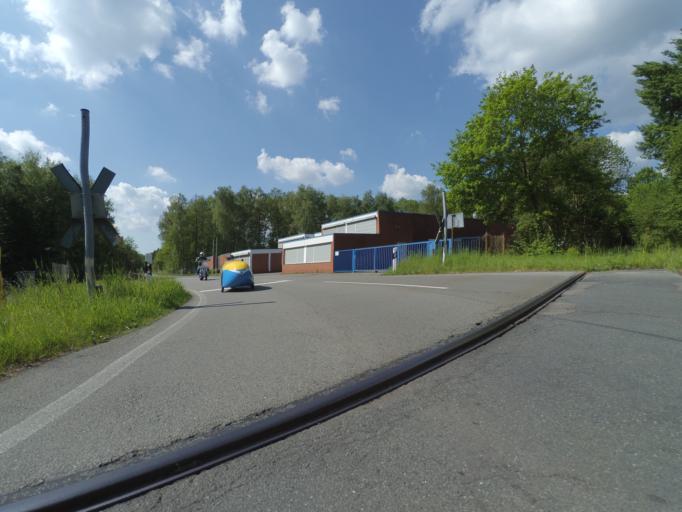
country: DE
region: Lower Saxony
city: Nienhagen
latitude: 52.5278
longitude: 10.0872
